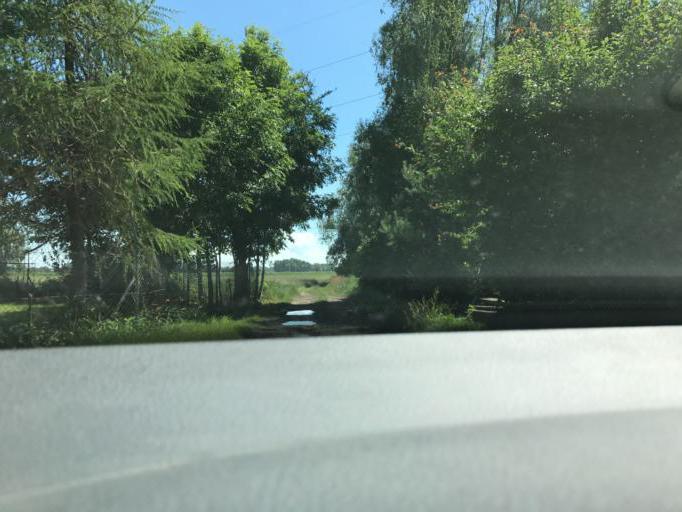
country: PL
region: Pomeranian Voivodeship
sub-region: Gdansk
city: Gdansk
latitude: 54.3207
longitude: 18.7516
